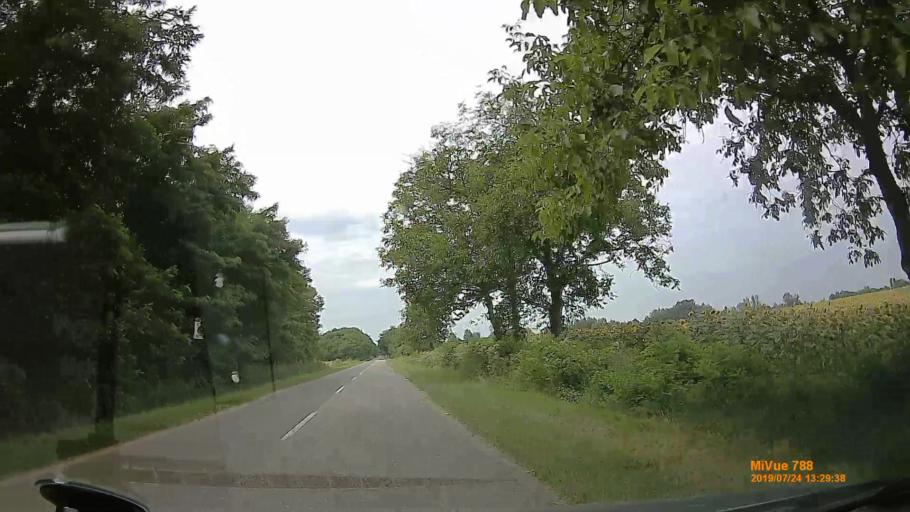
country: HU
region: Szabolcs-Szatmar-Bereg
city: Vasarosnameny
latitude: 48.2273
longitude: 22.3949
